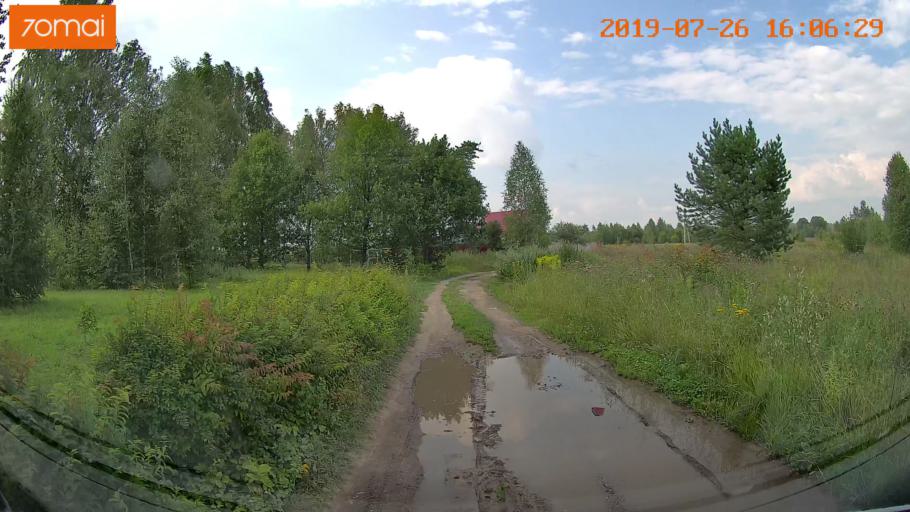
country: RU
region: Ivanovo
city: Bogorodskoye
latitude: 57.0593
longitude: 41.0559
